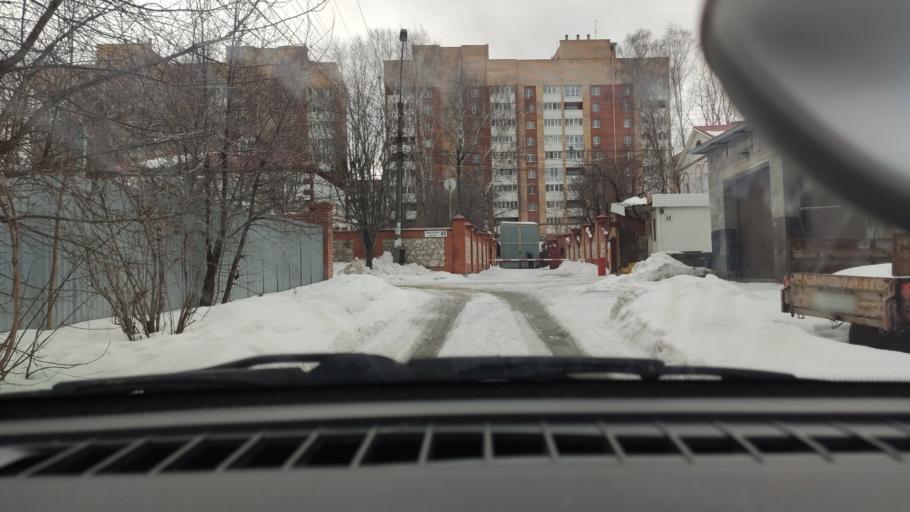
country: RU
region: Samara
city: Petra-Dubrava
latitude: 53.3115
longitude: 50.2881
